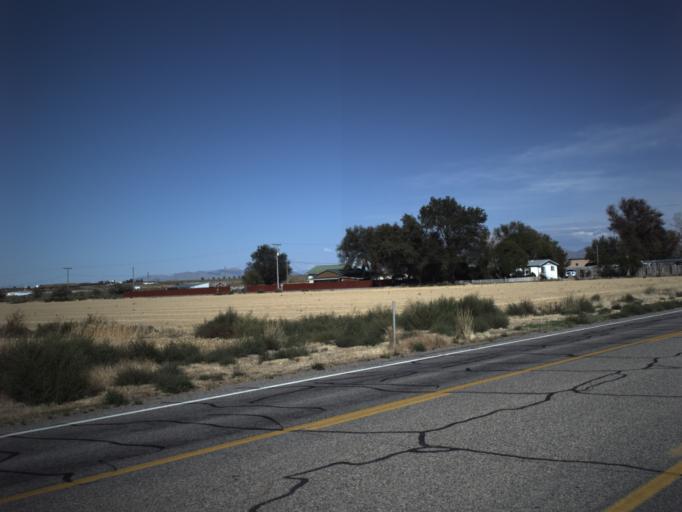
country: US
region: Utah
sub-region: Millard County
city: Delta
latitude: 39.3524
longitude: -112.5591
